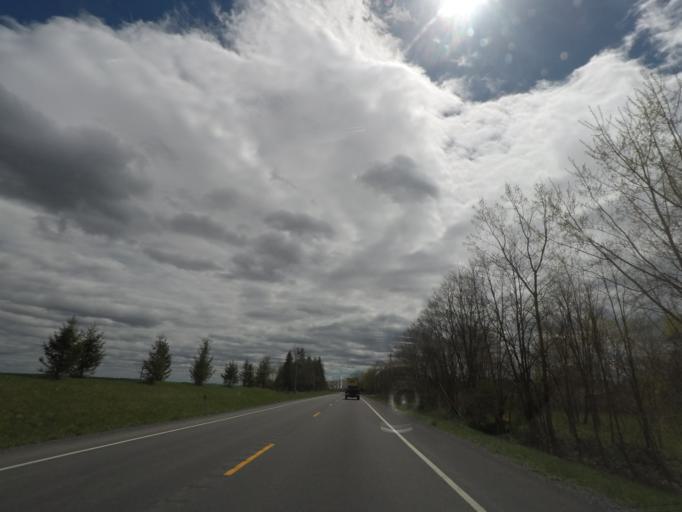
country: US
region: New York
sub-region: Albany County
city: Ravena
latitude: 42.4844
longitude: -73.7939
